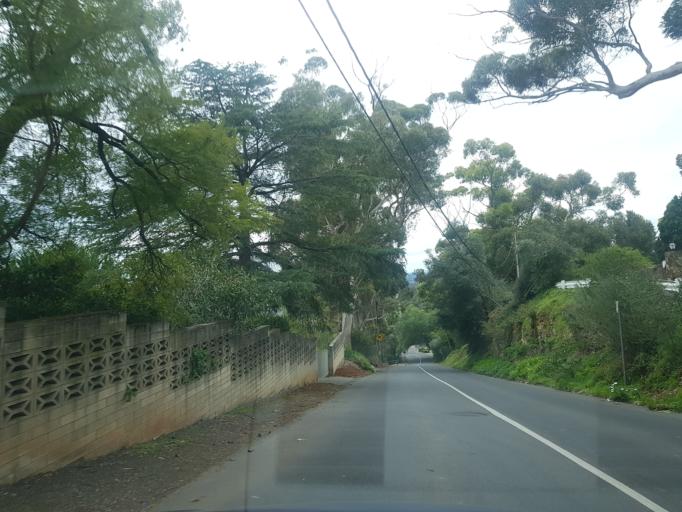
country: AU
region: South Australia
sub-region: Burnside
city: Mount Osmond
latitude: -34.9589
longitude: 138.6529
